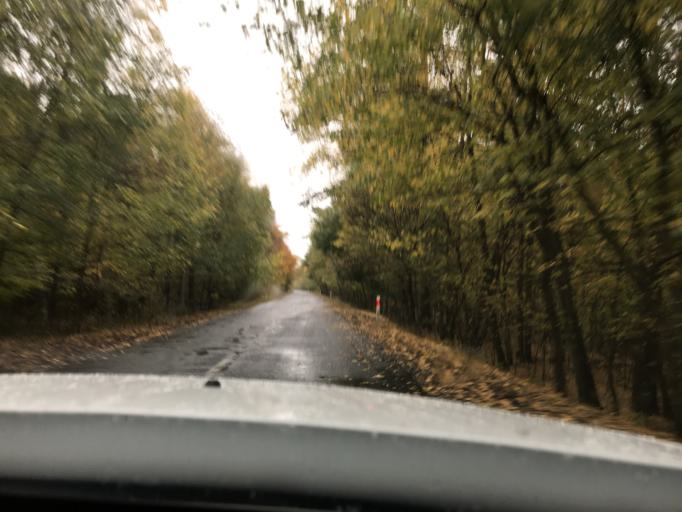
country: PL
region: West Pomeranian Voivodeship
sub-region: Powiat gryfinski
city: Mieszkowice
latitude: 52.7839
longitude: 14.4263
